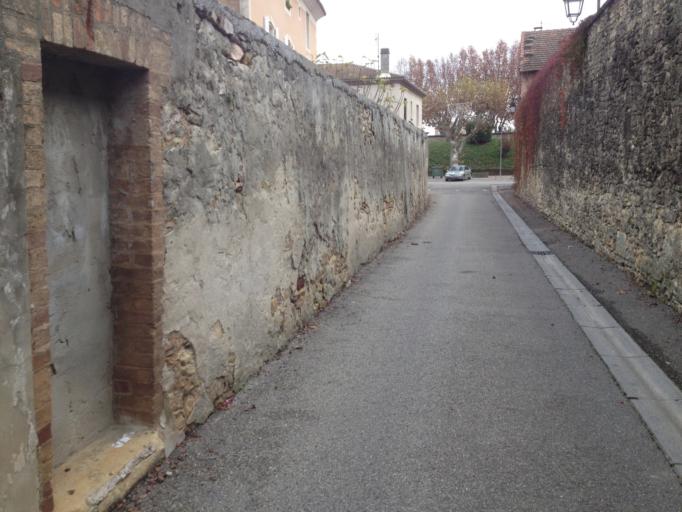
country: FR
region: Provence-Alpes-Cote d'Azur
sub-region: Departement du Vaucluse
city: Caderousse
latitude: 44.1006
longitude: 4.7568
